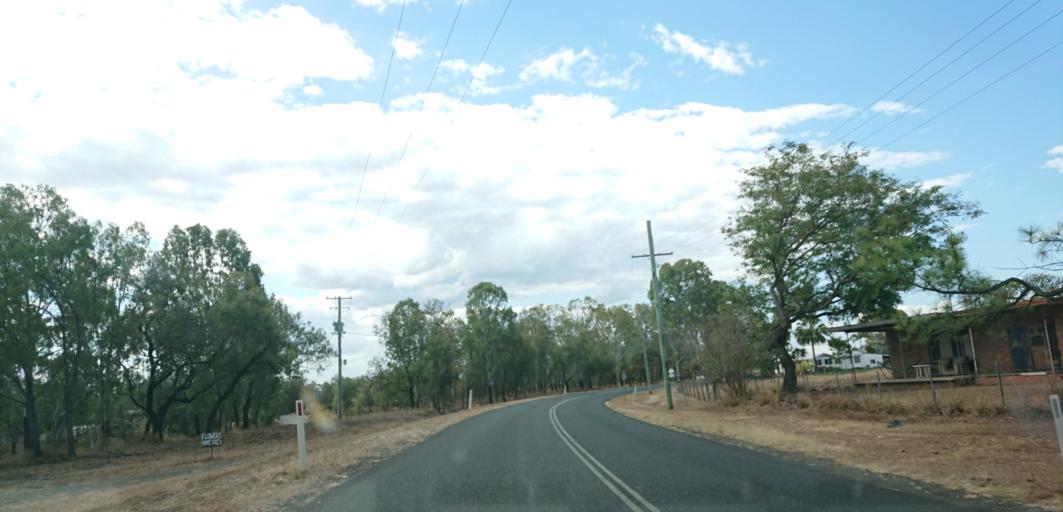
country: AU
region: Queensland
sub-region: Lockyer Valley
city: Gatton
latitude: -27.6079
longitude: 152.2095
